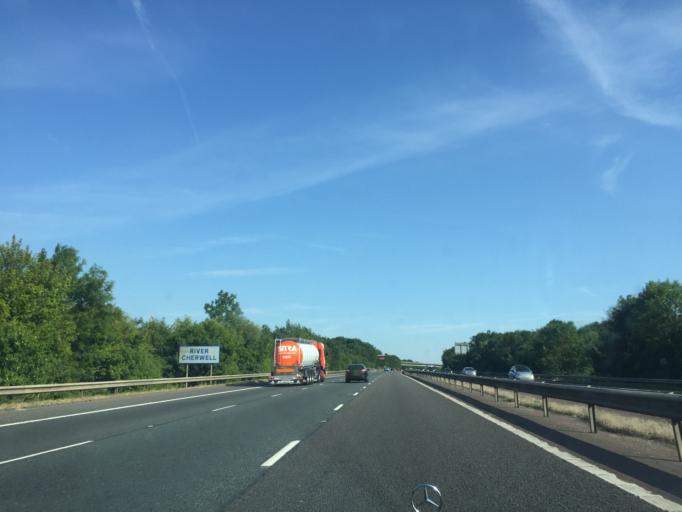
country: GB
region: England
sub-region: Oxfordshire
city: Adderbury
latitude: 52.0127
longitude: -1.2803
